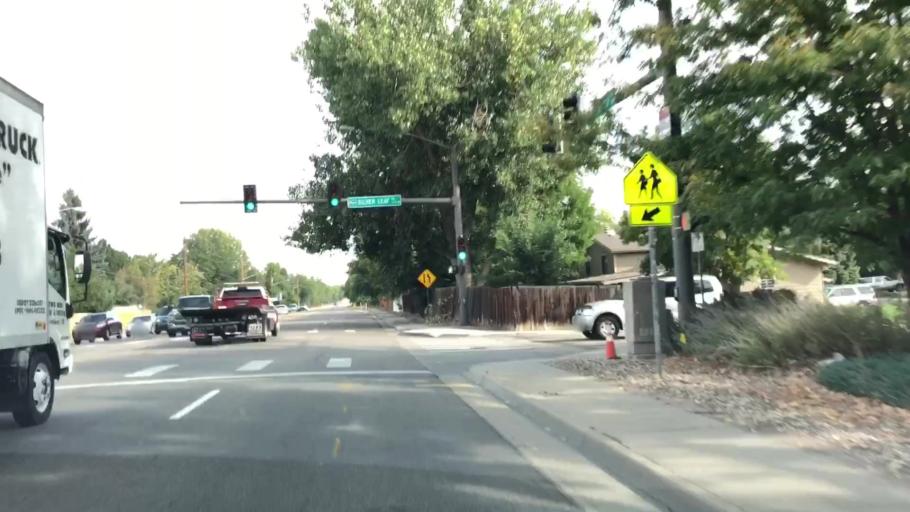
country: US
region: Colorado
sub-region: Larimer County
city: Loveland
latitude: 40.4160
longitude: -105.0586
